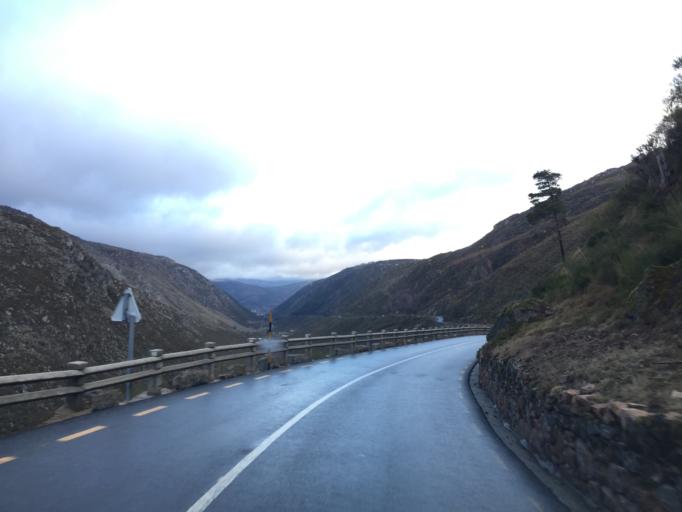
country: PT
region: Castelo Branco
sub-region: Covilha
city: Covilha
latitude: 40.3266
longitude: -7.5765
